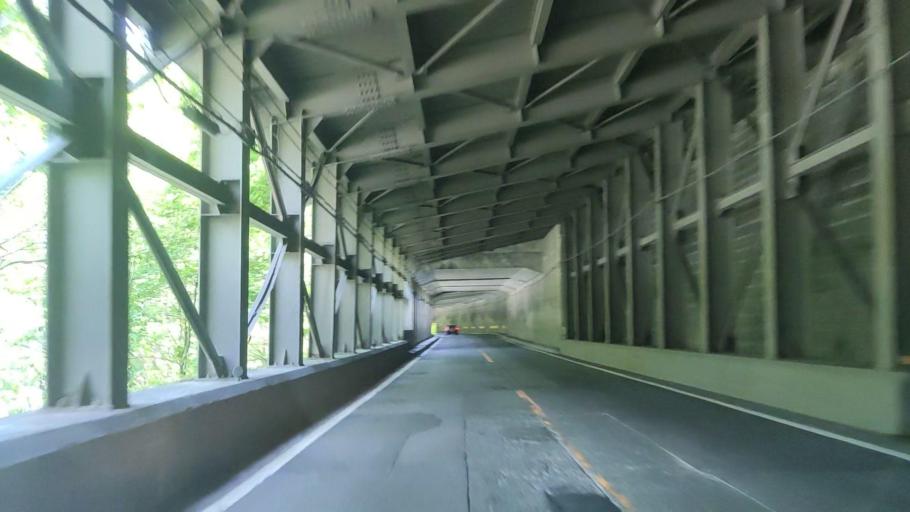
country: JP
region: Niigata
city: Itoigawa
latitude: 36.9058
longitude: 137.8641
